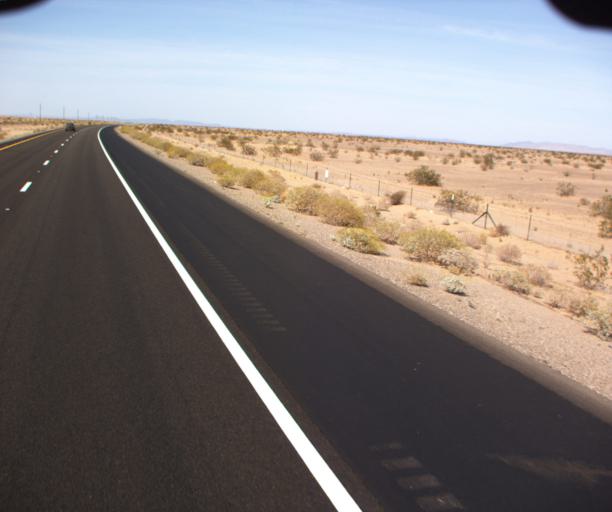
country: US
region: Arizona
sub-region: Yuma County
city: Somerton
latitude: 32.5180
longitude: -114.5615
